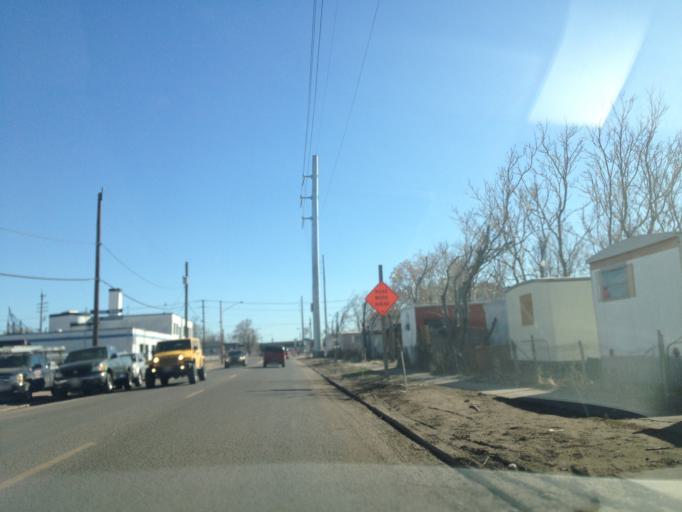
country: US
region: Colorado
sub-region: Adams County
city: Commerce City
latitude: 39.7837
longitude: -104.9594
